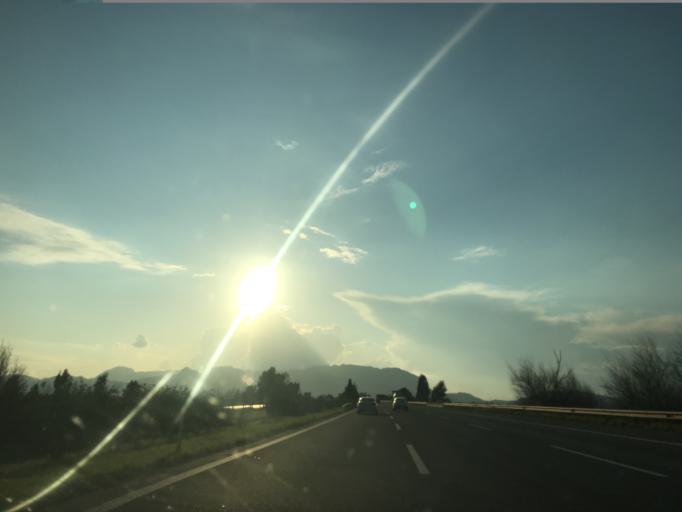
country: TR
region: Adana
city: Ceyhan
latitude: 36.9849
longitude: 35.8029
